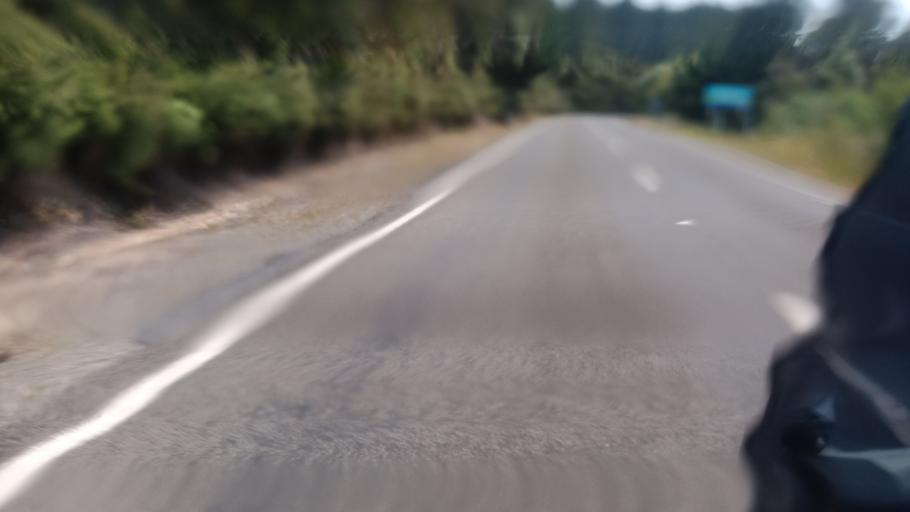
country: NZ
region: Bay of Plenty
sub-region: Opotiki District
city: Opotiki
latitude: -37.5742
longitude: 178.0648
